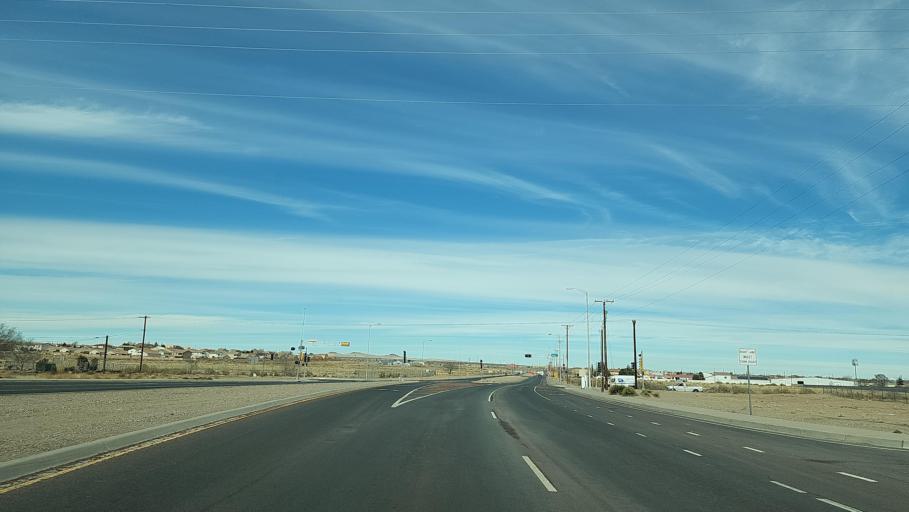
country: US
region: New Mexico
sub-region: Bernalillo County
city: South Valley
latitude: 35.0594
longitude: -106.7073
